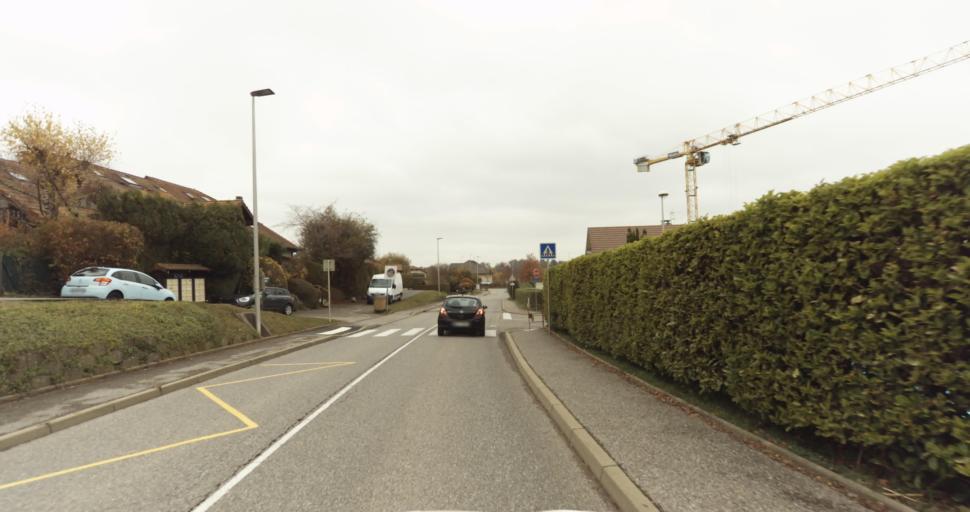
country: FR
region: Rhone-Alpes
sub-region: Departement de la Haute-Savoie
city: Seynod
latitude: 45.8626
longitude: 6.0885
